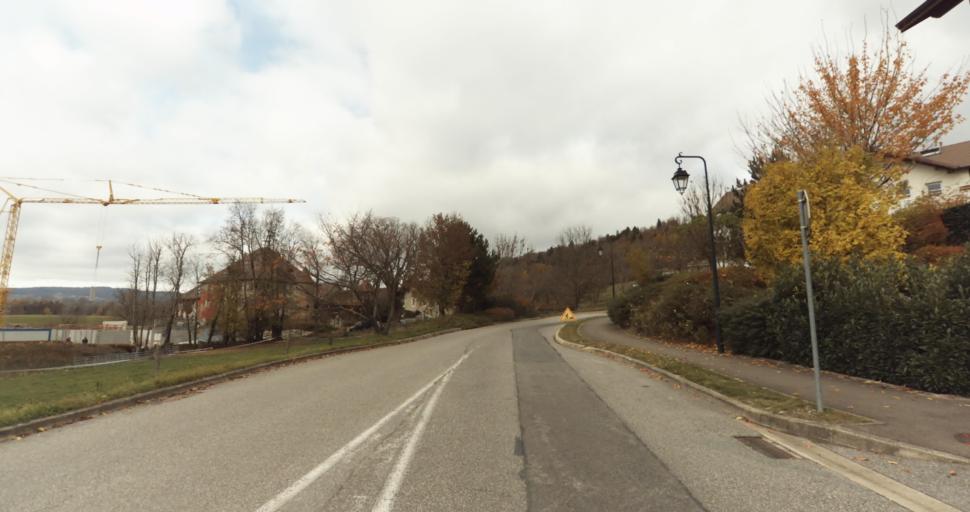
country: FR
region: Rhone-Alpes
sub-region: Departement de la Haute-Savoie
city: Pringy
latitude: 45.9446
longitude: 6.1375
